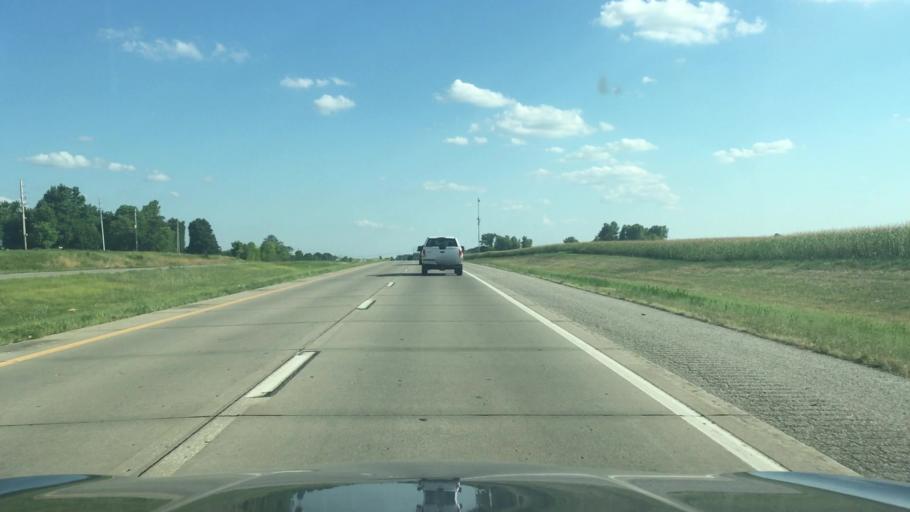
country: US
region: Missouri
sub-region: Jackson County
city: Lees Summit
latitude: 38.8768
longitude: -94.3745
